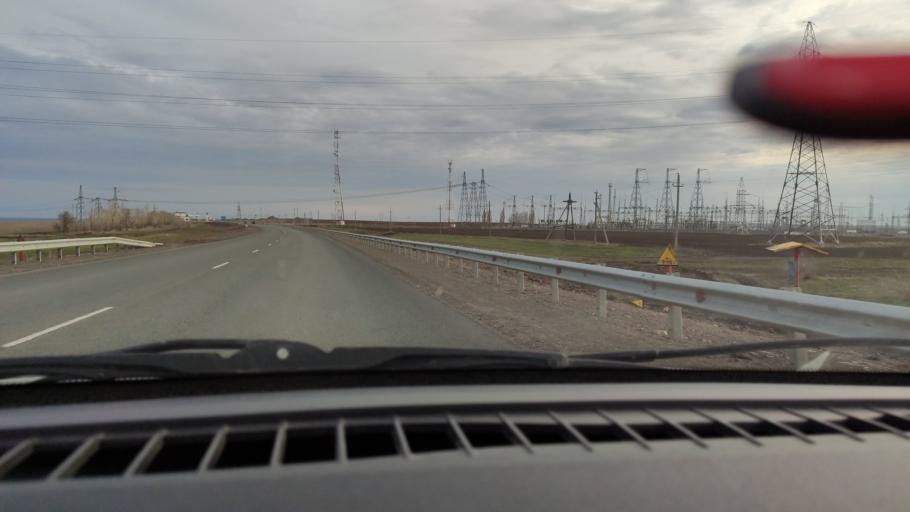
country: RU
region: Orenburg
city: Tatarskaya Kargala
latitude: 51.9828
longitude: 55.1877
